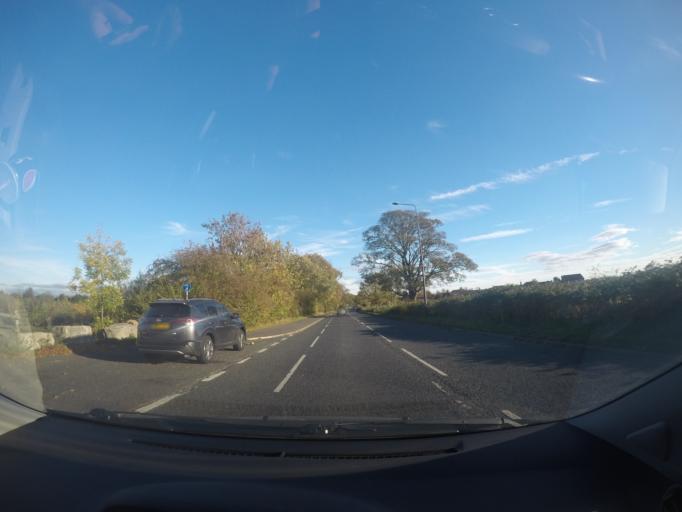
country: GB
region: England
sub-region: City of York
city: Nether Poppleton
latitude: 53.9716
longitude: -1.1381
